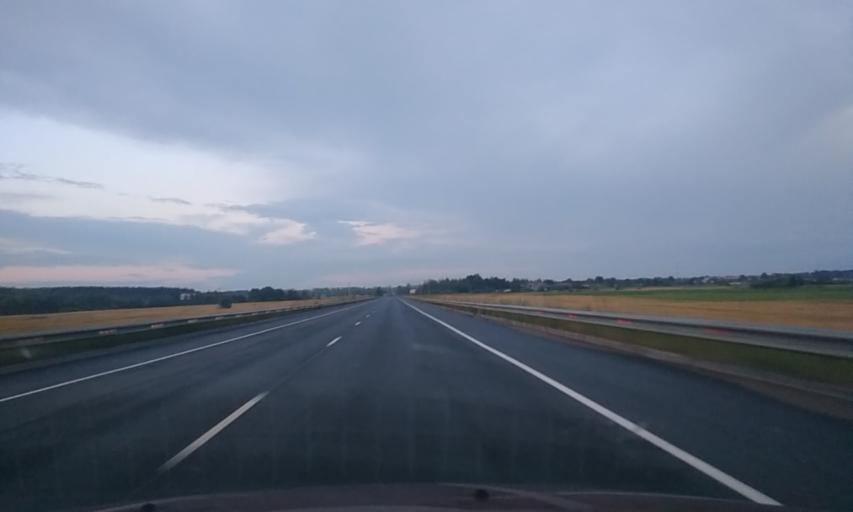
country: RU
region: Vladimir
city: Murom
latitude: 55.5878
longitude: 41.9660
